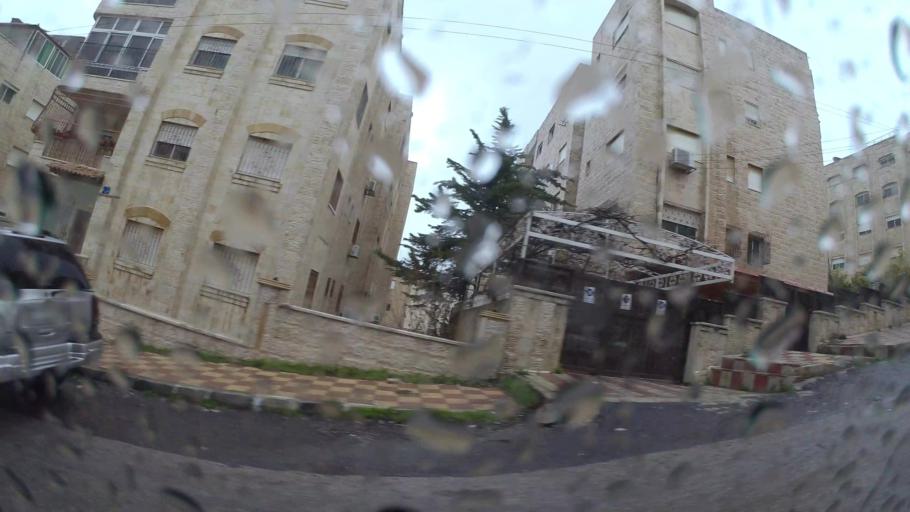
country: JO
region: Amman
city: Al Jubayhah
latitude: 32.0148
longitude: 35.8809
